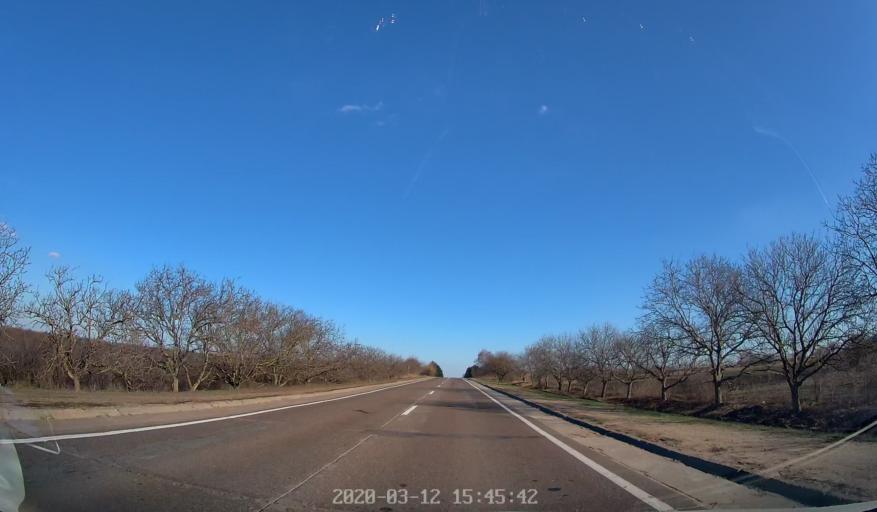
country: MD
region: Chisinau
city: Stauceni
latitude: 47.1042
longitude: 28.8798
